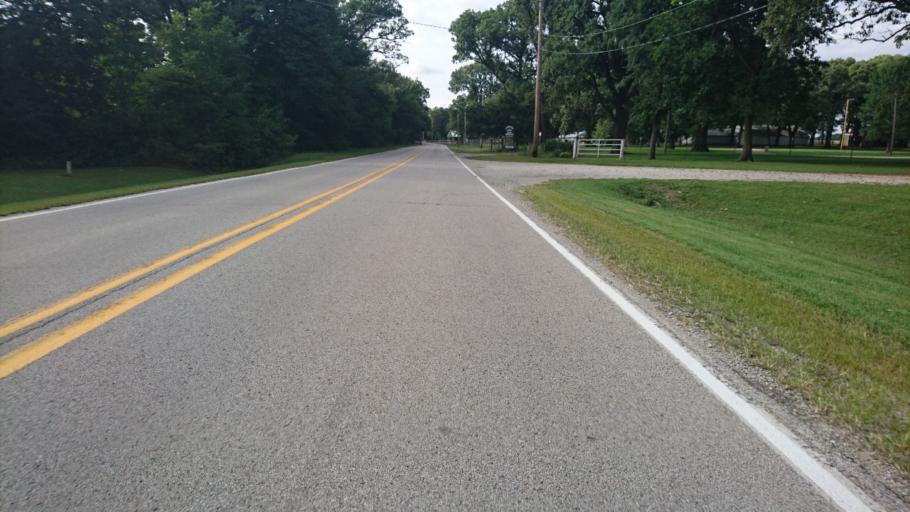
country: US
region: Illinois
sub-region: Livingston County
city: Pontiac
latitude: 40.8898
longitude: -88.6627
